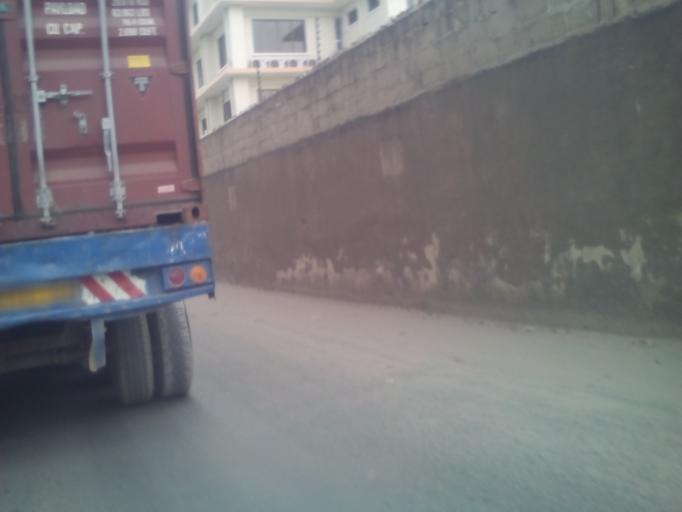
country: TZ
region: Dar es Salaam
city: Dar es Salaam
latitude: -6.8529
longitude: 39.2304
